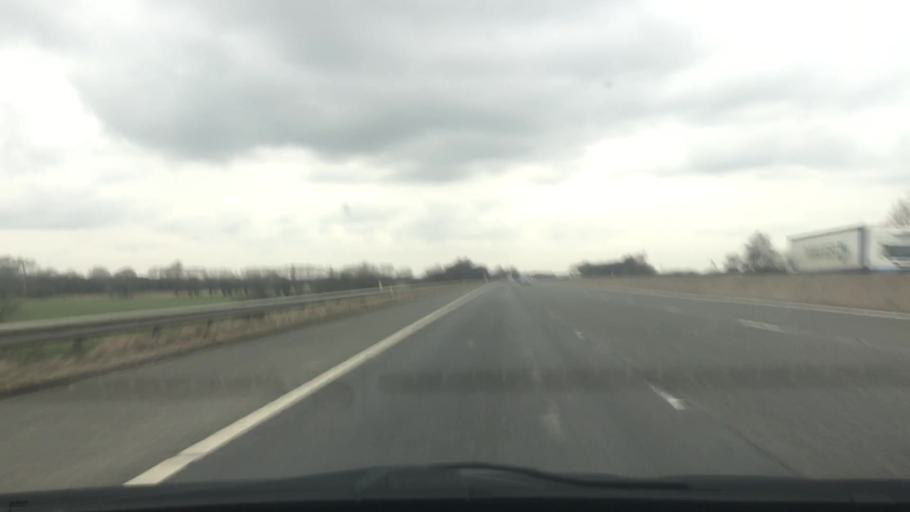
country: GB
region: England
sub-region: North Lincolnshire
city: Crowle
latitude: 53.5725
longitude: -0.8990
